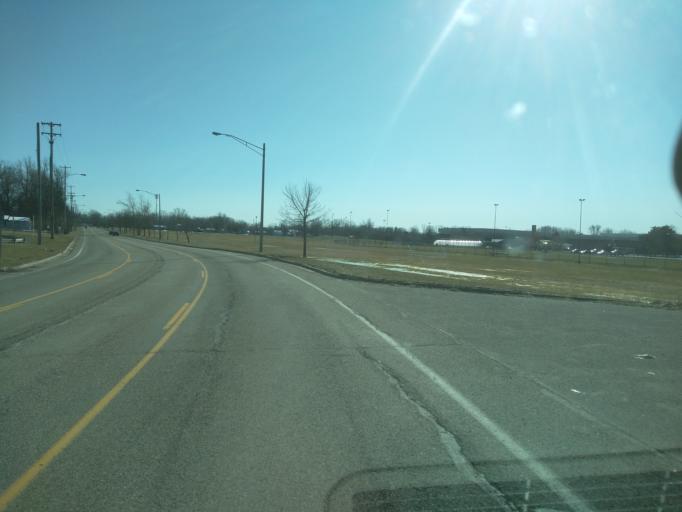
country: US
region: Michigan
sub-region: Ingham County
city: Lansing
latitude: 42.6765
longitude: -84.5872
